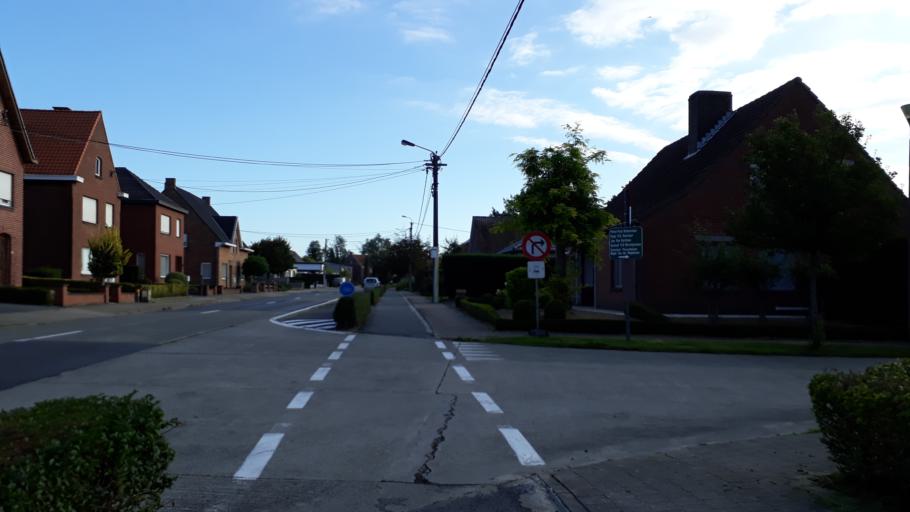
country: BE
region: Flanders
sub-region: Provincie West-Vlaanderen
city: Torhout
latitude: 51.0722
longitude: 3.1119
